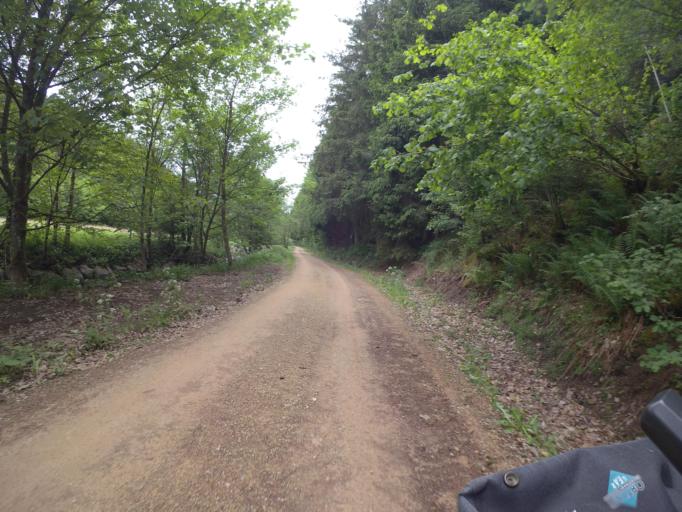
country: DE
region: North Rhine-Westphalia
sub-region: Regierungsbezirk Koln
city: Hellenthal
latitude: 50.4388
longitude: 6.4087
